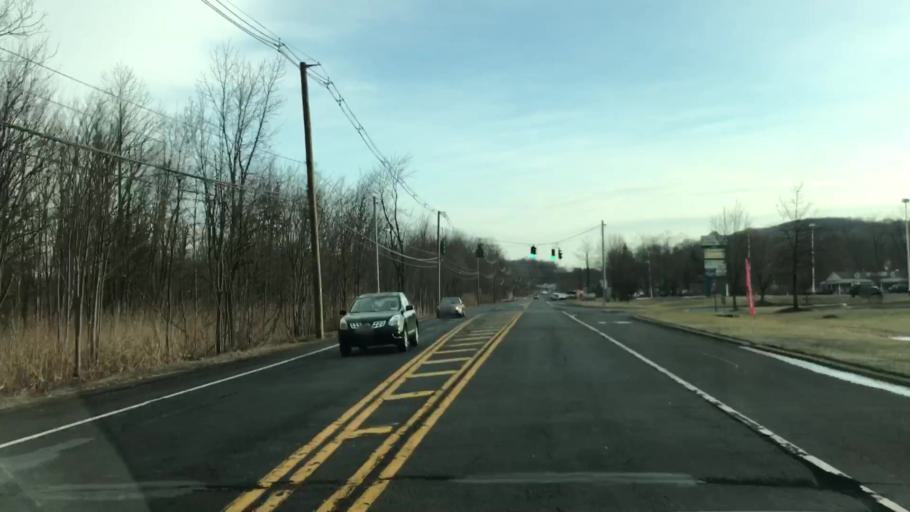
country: US
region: New York
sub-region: Rockland County
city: Mount Ivy
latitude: 41.1831
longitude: -74.0482
